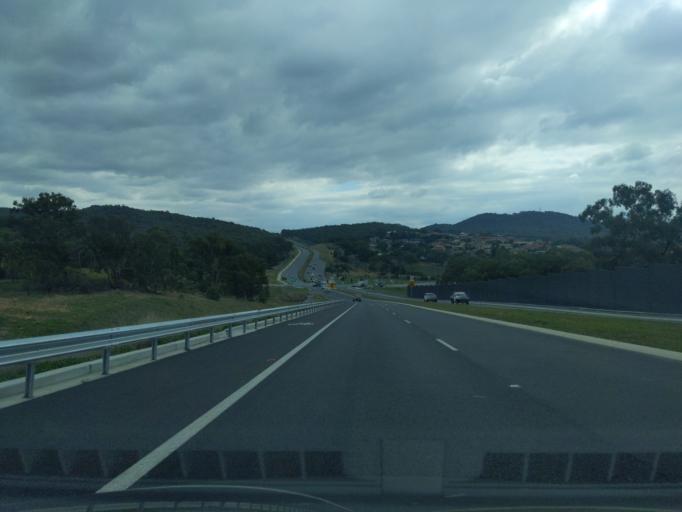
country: AU
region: New South Wales
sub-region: Queanbeyan
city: Queanbeyan
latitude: -35.3786
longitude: 149.2394
